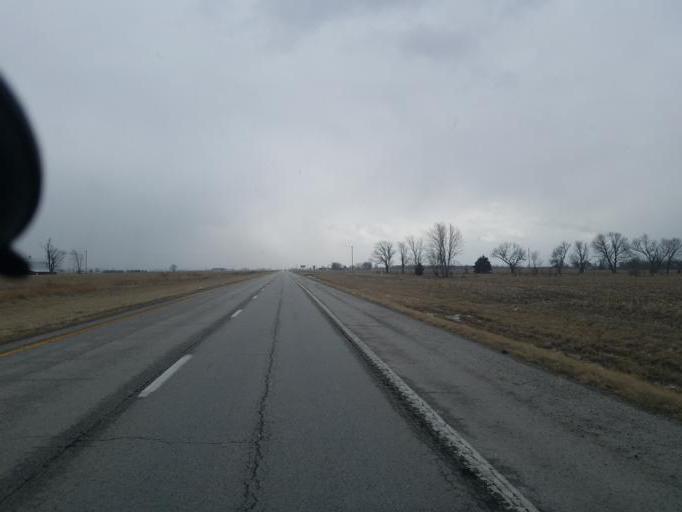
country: US
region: Missouri
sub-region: Randolph County
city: Huntsville
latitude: 39.5712
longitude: -92.4648
